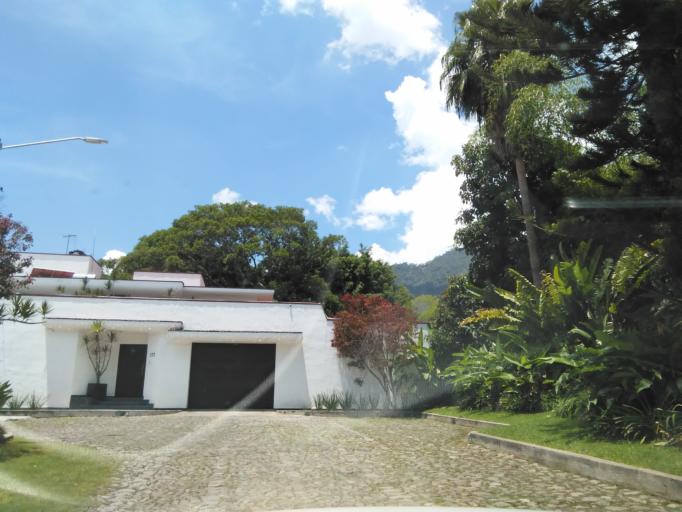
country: MX
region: Nayarit
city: Tepic
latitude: 21.5048
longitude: -104.9138
